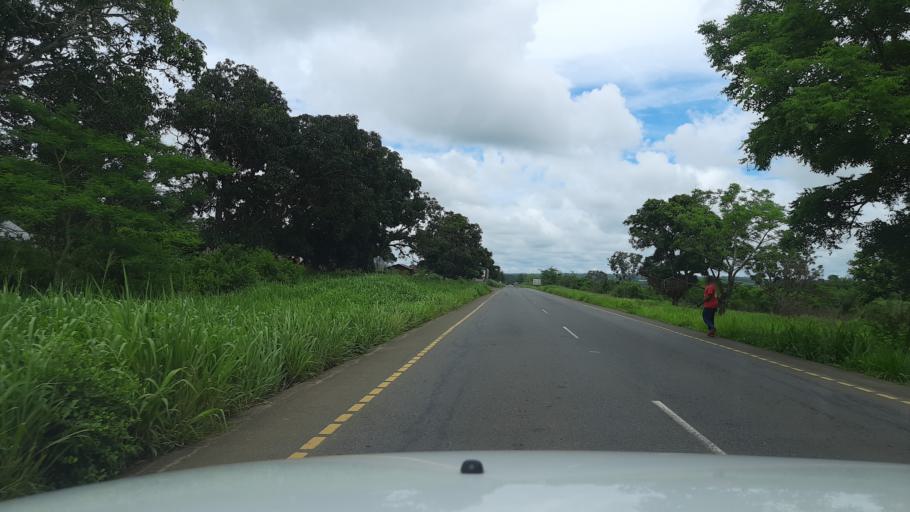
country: TZ
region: Pwani
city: Lugoba
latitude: -5.9356
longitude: 38.2264
